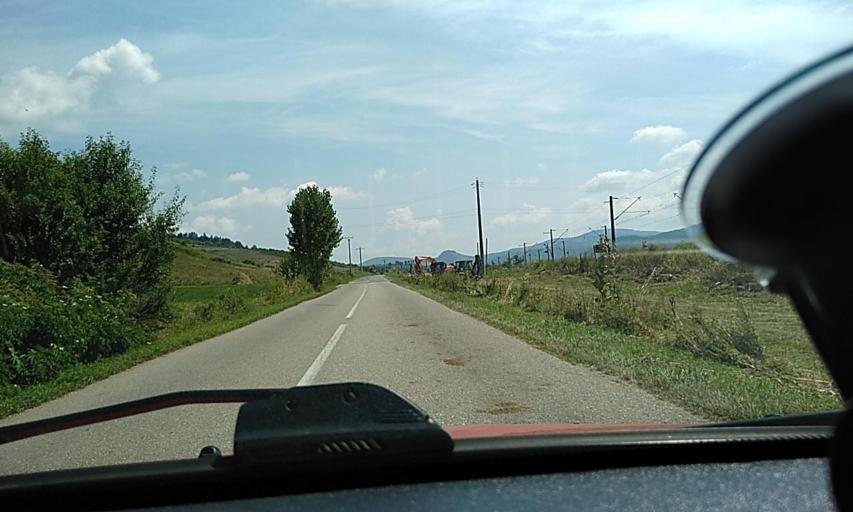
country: RO
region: Brasov
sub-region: Comuna Hoghiz
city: Hoghiz
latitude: 46.0290
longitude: 25.3811
